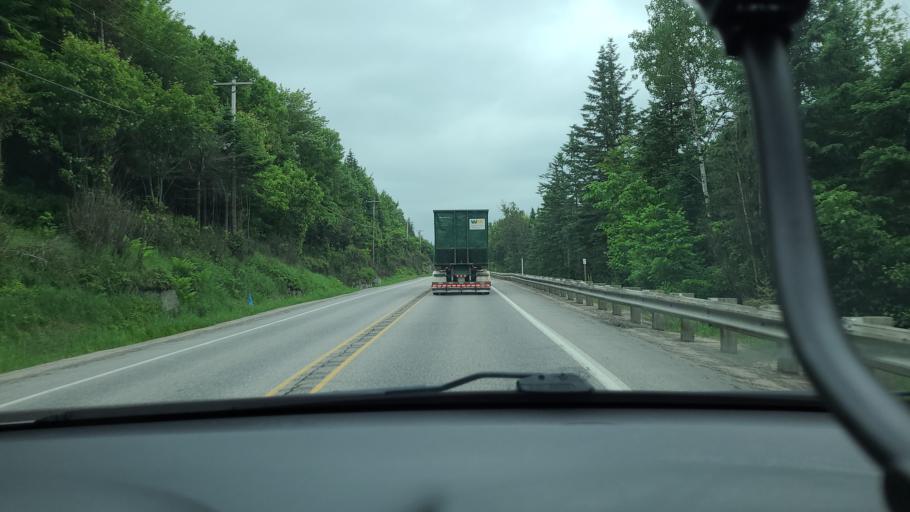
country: CA
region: Quebec
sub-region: Laurentides
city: Labelle
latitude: 46.3038
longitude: -74.7845
